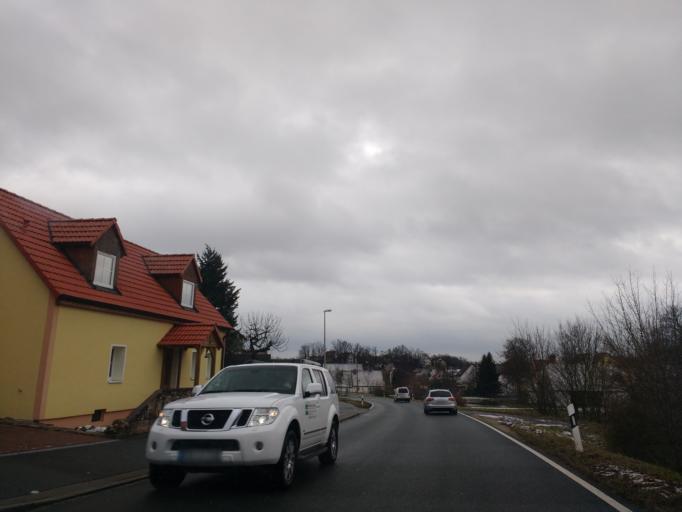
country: DE
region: Bavaria
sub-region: Regierungsbezirk Mittelfranken
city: Herzogenaurach
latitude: 49.5867
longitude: 10.8577
